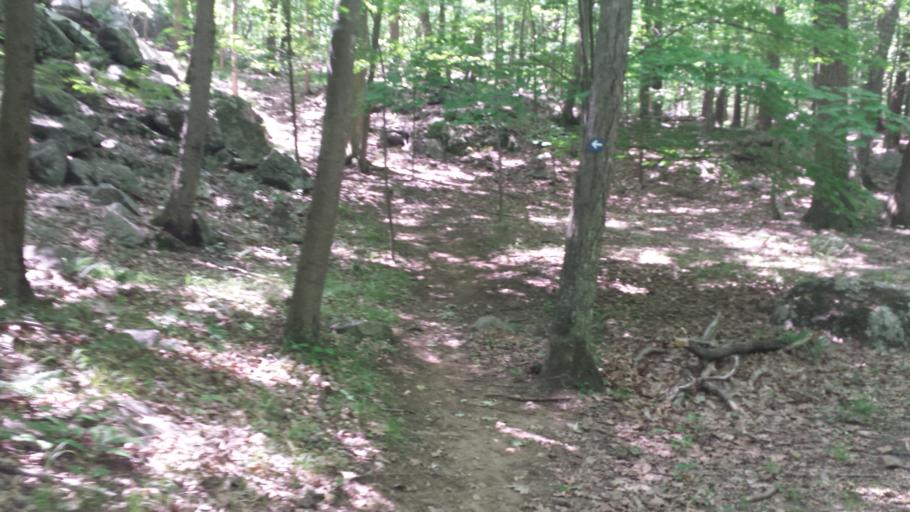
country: US
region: New York
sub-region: Putnam County
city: Peach Lake
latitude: 41.3136
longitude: -73.5605
